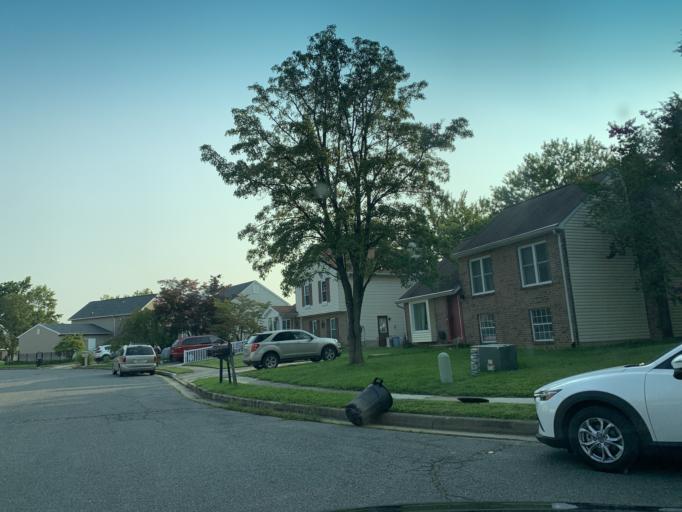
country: US
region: Maryland
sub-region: Baltimore County
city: Bowleys Quarters
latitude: 39.3705
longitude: -76.3558
